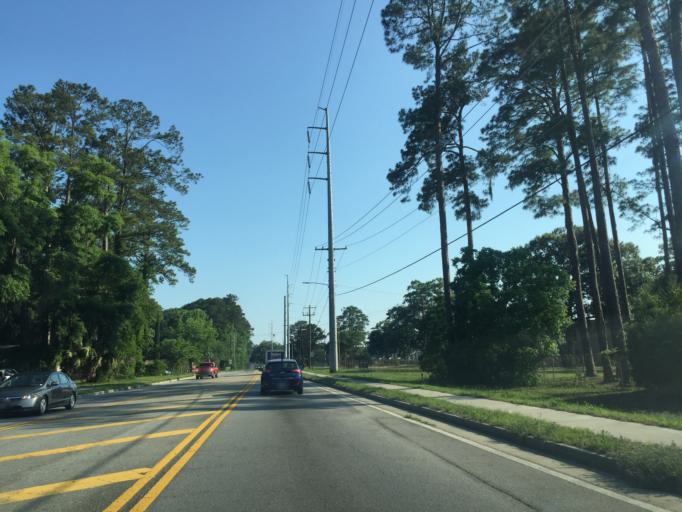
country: US
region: Georgia
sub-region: Chatham County
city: Isle of Hope
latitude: 31.9988
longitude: -81.0778
